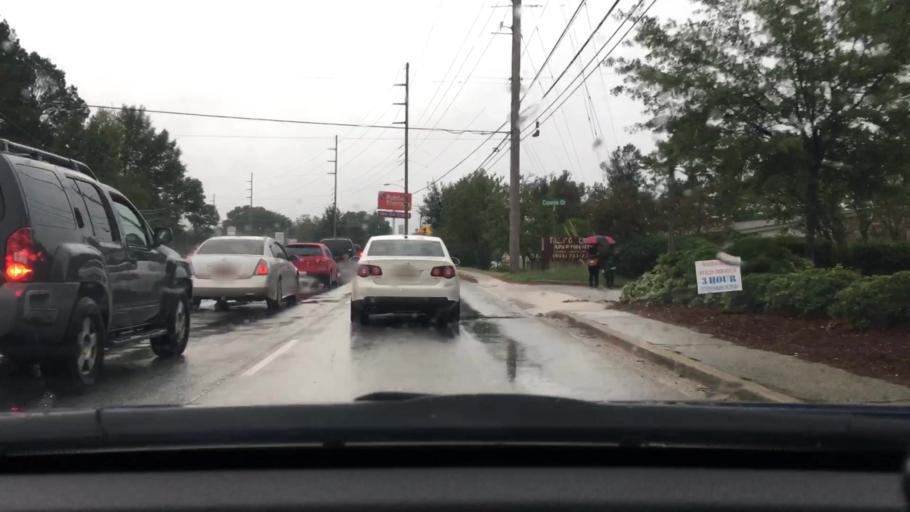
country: US
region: South Carolina
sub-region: Lexington County
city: Saint Andrews
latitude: 34.0549
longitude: -81.1102
